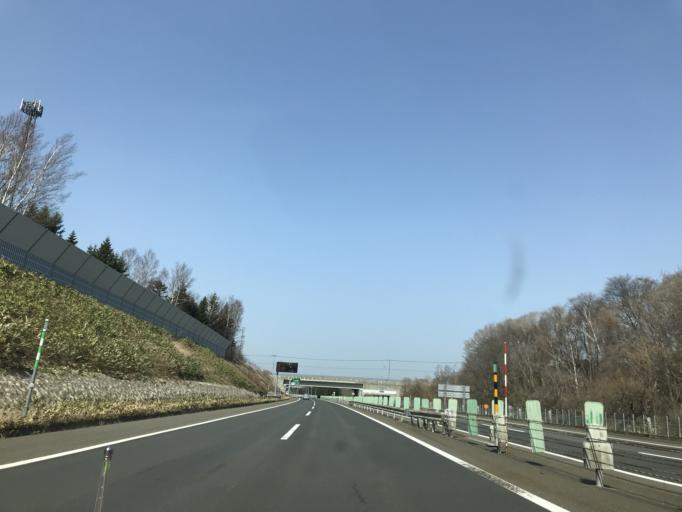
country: JP
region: Hokkaido
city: Ebetsu
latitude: 43.0911
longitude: 141.5055
